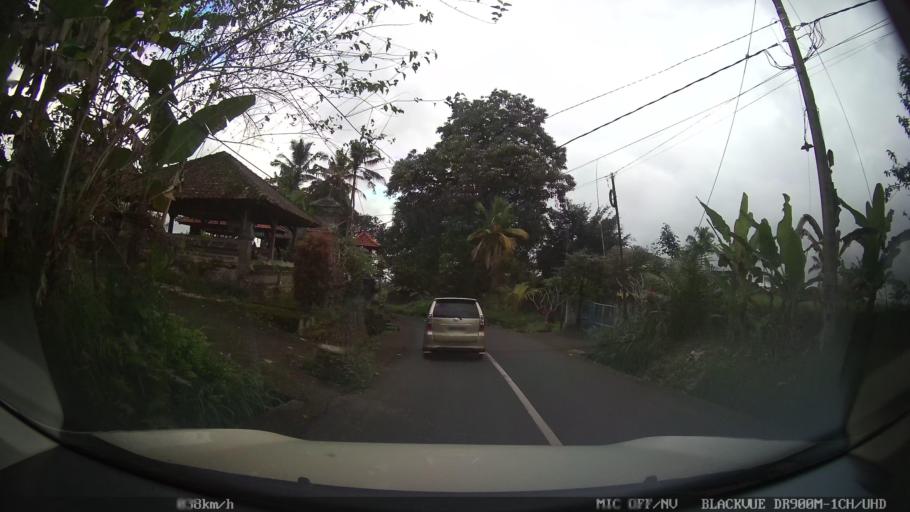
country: ID
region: Bali
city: Peneng
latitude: -8.3565
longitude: 115.1849
